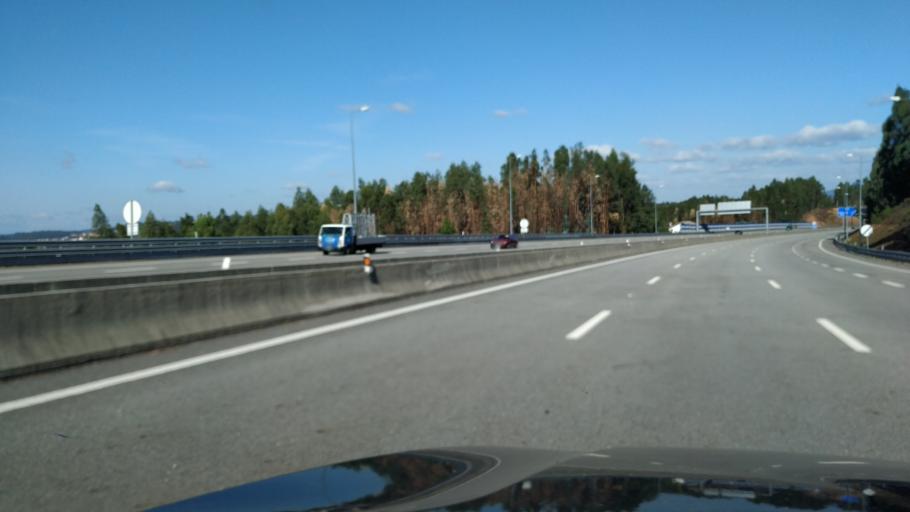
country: PT
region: Aveiro
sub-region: Santa Maria da Feira
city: Lobao
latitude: 41.0174
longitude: -8.4784
